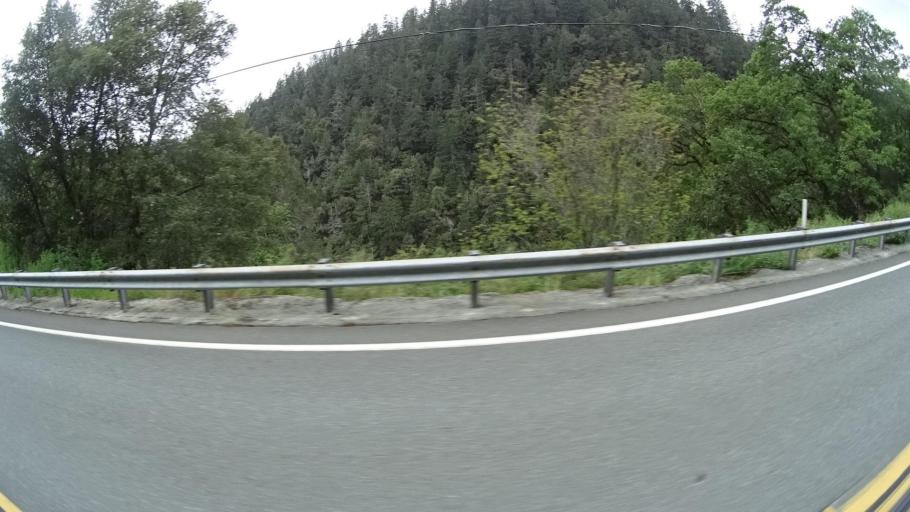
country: US
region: California
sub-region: Humboldt County
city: Willow Creek
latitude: 41.1130
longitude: -123.6871
